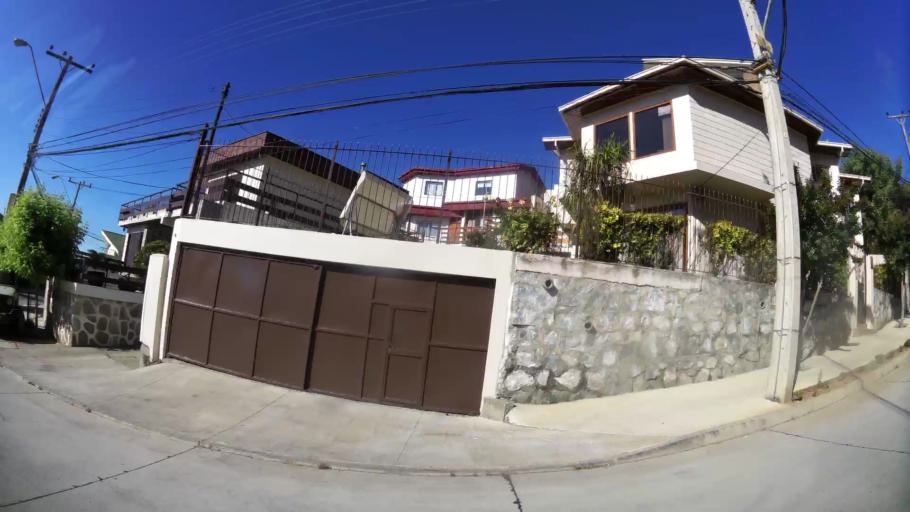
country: CL
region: Valparaiso
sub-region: Provincia de Valparaiso
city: Vina del Mar
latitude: -33.0346
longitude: -71.5602
